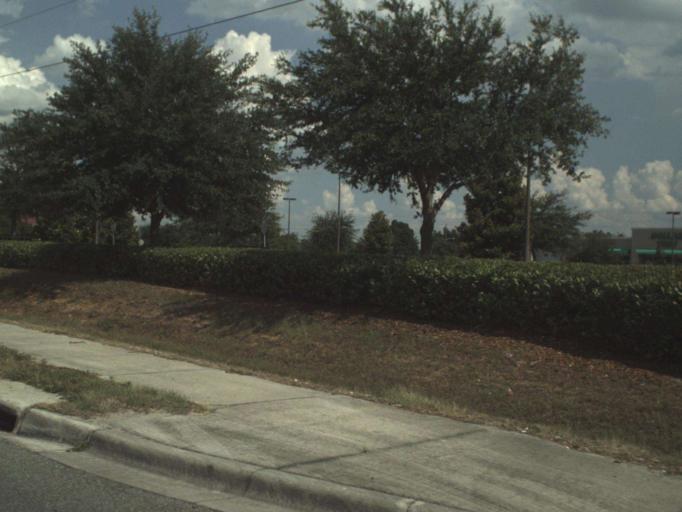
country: US
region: Florida
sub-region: Lake County
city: Tavares
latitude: 28.8218
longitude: -81.6989
